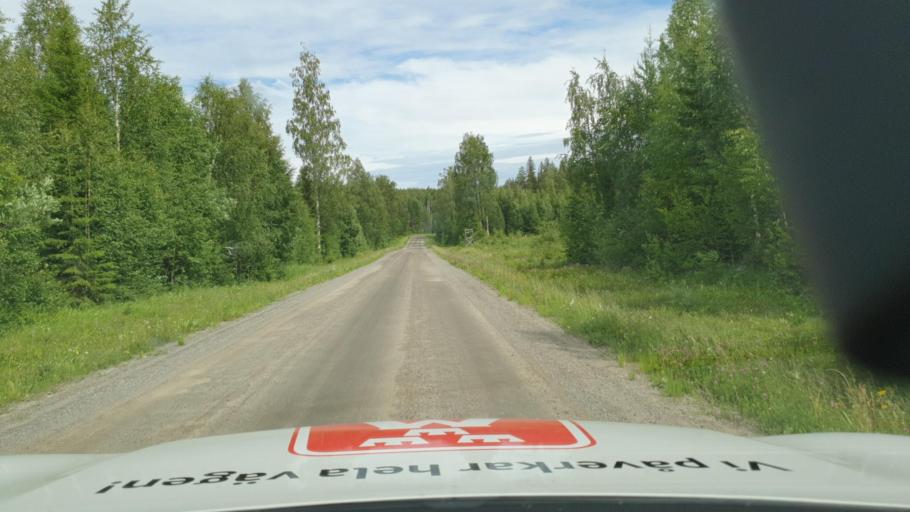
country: SE
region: Vaesterbotten
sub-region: Skelleftea Kommun
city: Burtraesk
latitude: 64.4919
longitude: 20.5859
